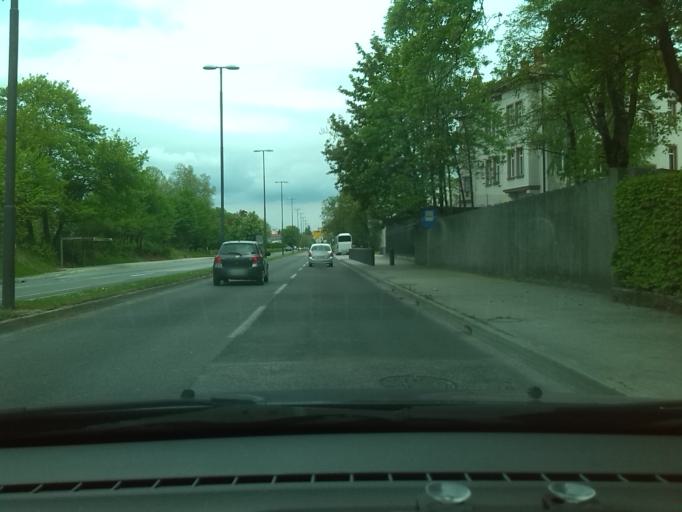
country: SI
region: Ljubljana
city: Ljubljana
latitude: 46.0524
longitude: 14.4975
